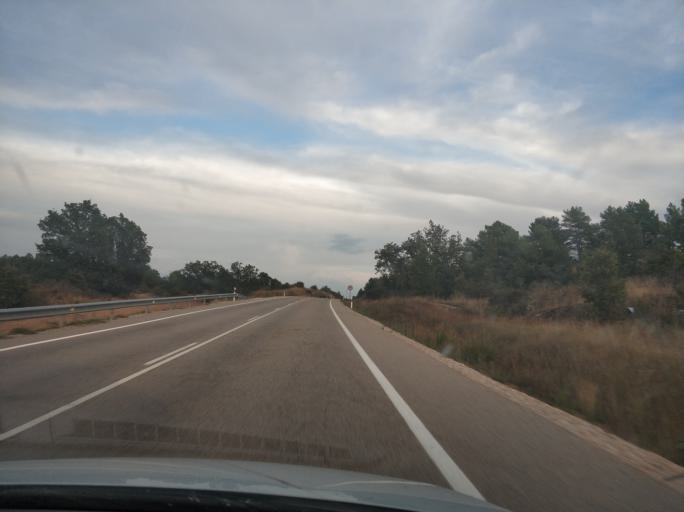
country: ES
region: Castille and Leon
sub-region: Provincia de Burgos
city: Cabezon de la Sierra
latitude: 41.8950
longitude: -3.2599
